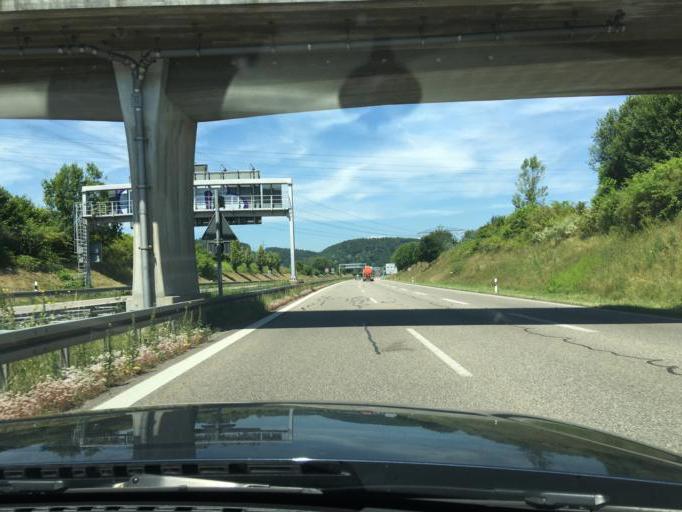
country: DE
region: Baden-Wuerttemberg
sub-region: Freiburg Region
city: Rheinfelden (Baden)
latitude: 47.5549
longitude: 7.7574
